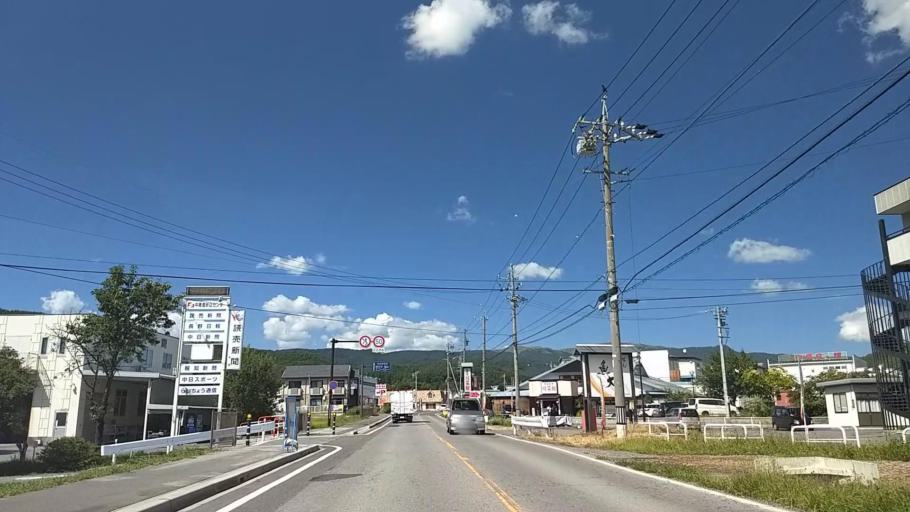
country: JP
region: Nagano
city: Chino
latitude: 36.0071
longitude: 138.1751
